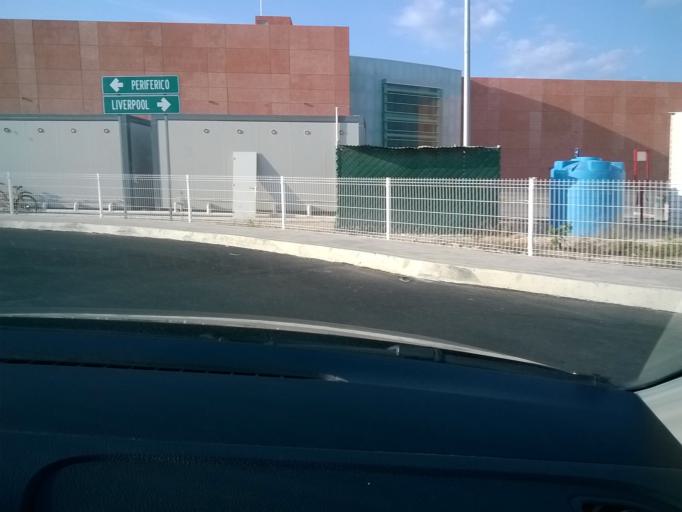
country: MX
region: Yucatan
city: Merida
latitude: 21.0382
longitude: -89.6324
